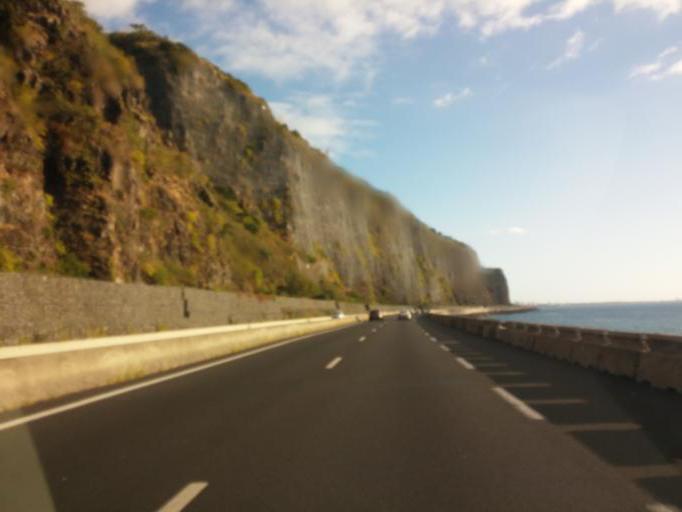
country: RE
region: Reunion
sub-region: Reunion
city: La Possession
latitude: -20.9056
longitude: 55.3636
